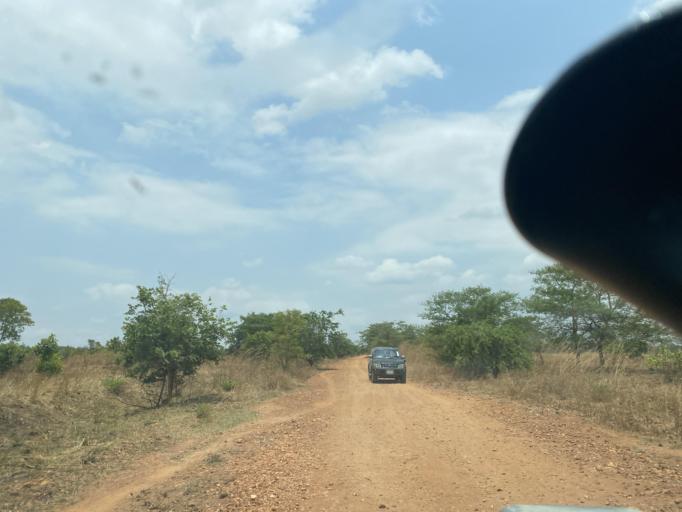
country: ZM
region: Lusaka
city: Chongwe
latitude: -15.5318
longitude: 28.8258
